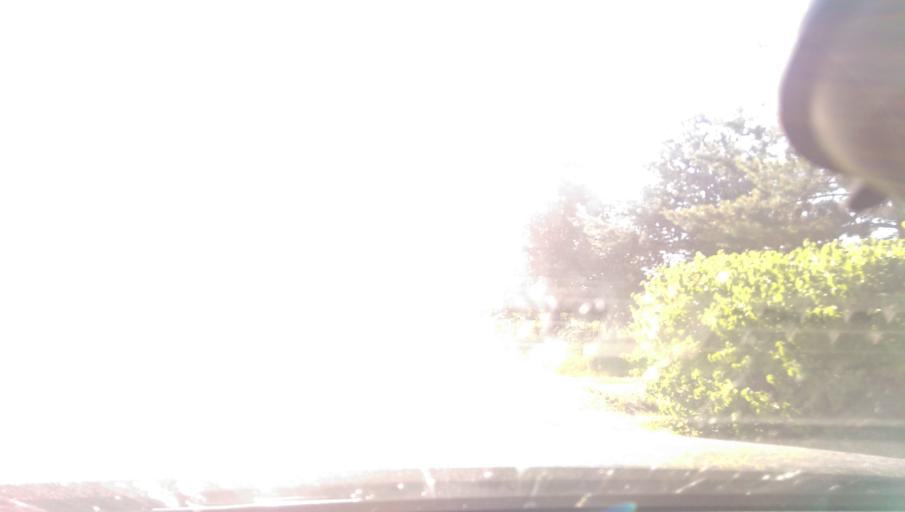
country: LT
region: Klaipedos apskritis
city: Gargzdai
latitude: 55.7125
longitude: 21.3707
